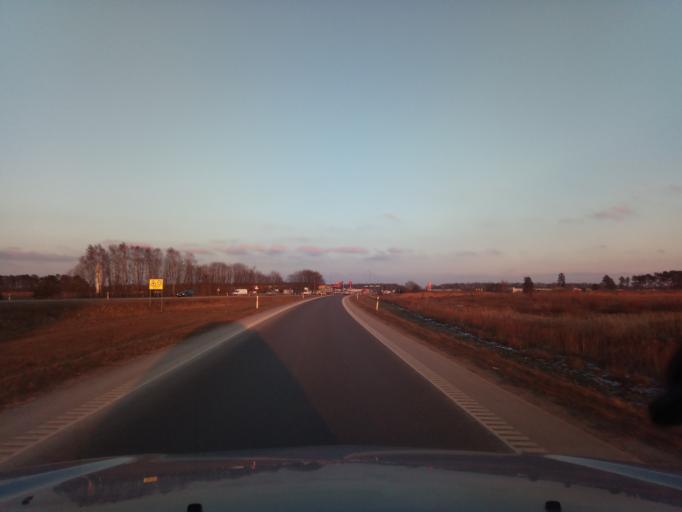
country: LT
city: Lentvaris
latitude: 54.6210
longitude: 25.1007
